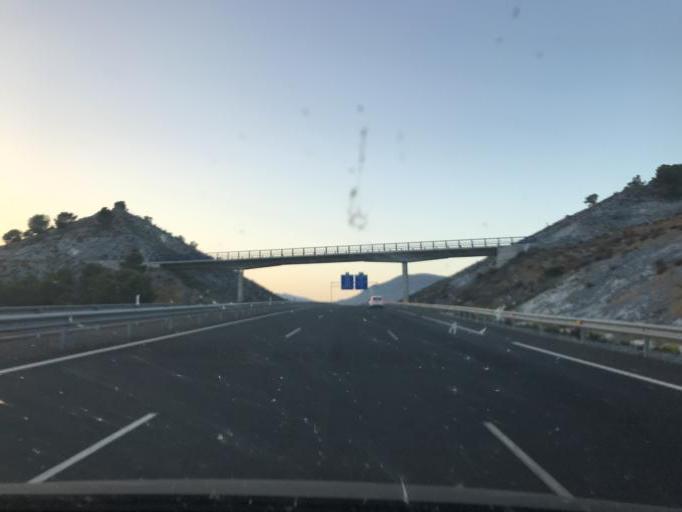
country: ES
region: Andalusia
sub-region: Provincia de Granada
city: Motril
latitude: 36.7759
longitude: -3.4965
